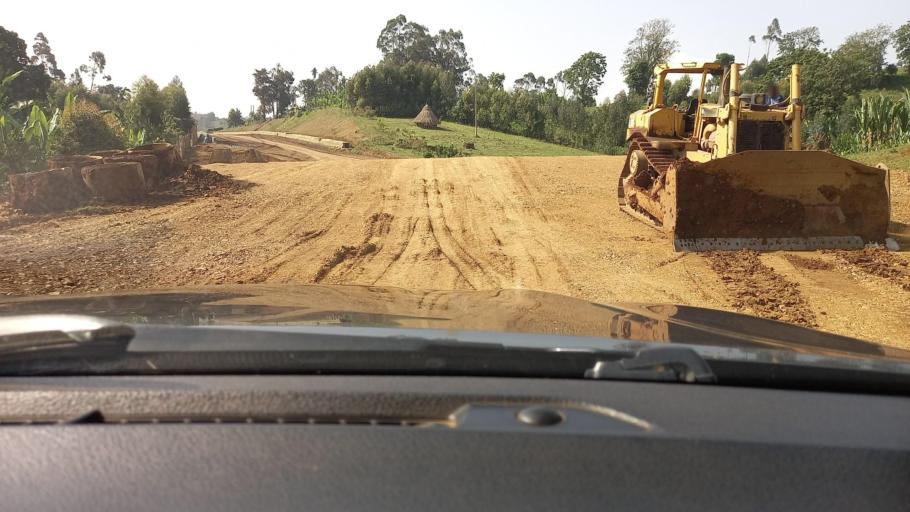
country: ET
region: Southern Nations, Nationalities, and People's Region
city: Mizan Teferi
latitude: 6.1682
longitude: 35.5848
